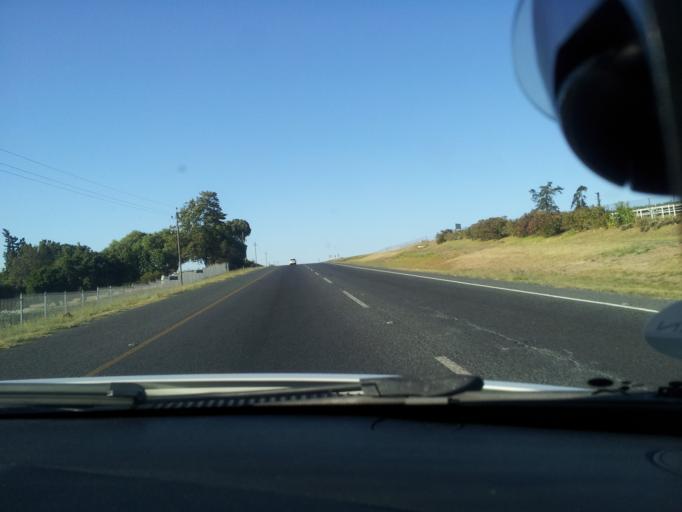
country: ZA
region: Western Cape
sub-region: Cape Winelands District Municipality
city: Stellenbosch
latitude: -34.0215
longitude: 18.8202
